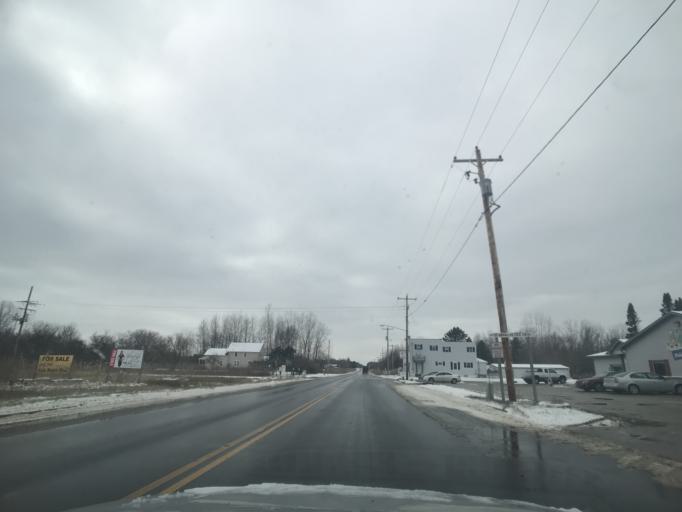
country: US
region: Wisconsin
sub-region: Brown County
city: Suamico
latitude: 44.7209
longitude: -88.0699
